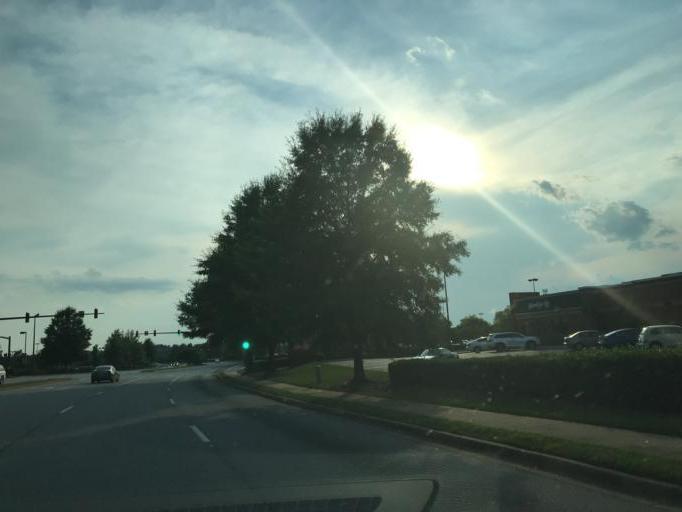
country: US
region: Alabama
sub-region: Russell County
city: Phenix City
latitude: 32.5471
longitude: -84.9412
